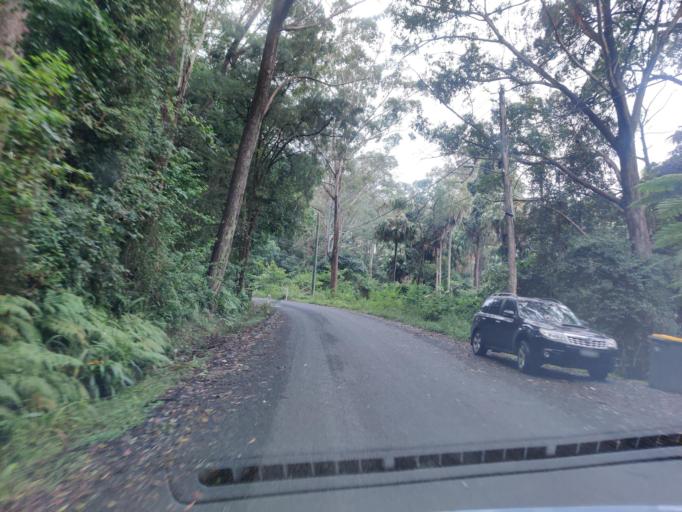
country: AU
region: New South Wales
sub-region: Great Lakes
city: Forster
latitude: -32.3866
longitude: 152.5026
